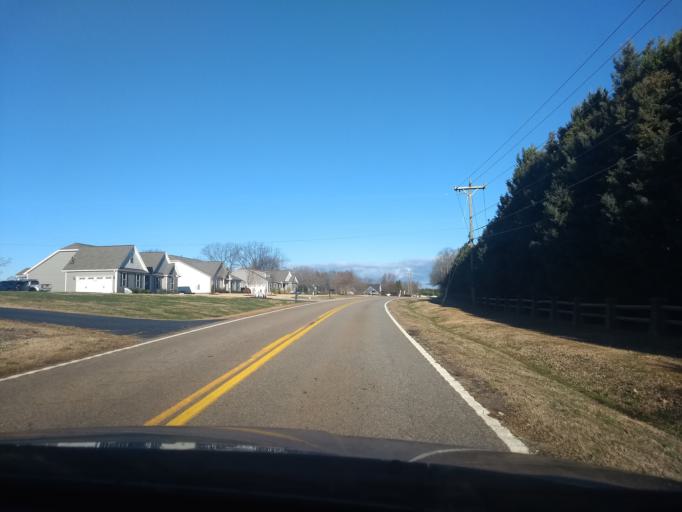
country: US
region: South Carolina
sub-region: Greenville County
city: Greer
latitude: 34.9832
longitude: -82.1991
